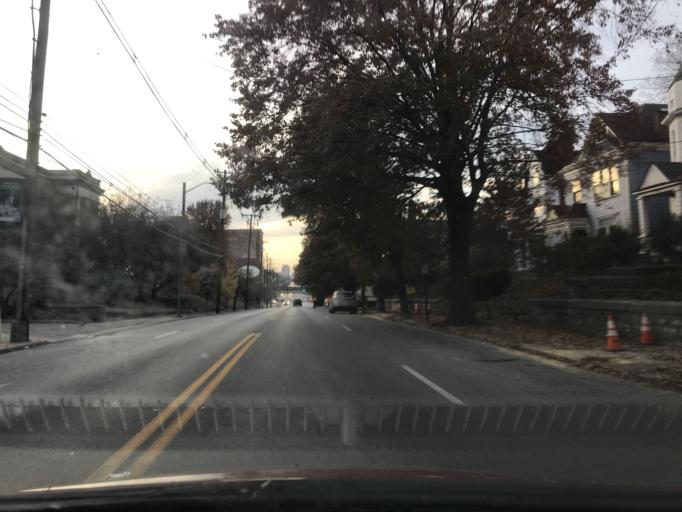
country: US
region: Kentucky
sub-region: Jefferson County
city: Louisville
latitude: 38.2441
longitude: -85.7318
